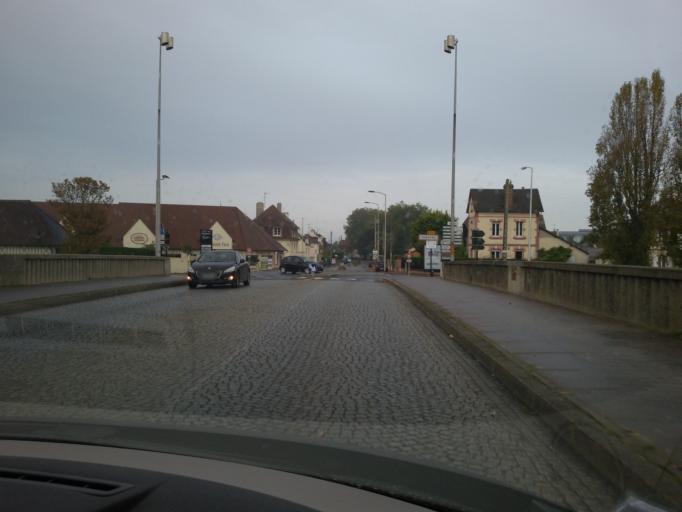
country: FR
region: Lower Normandy
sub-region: Departement du Calvados
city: Cabourg
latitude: 49.2858
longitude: -0.1117
